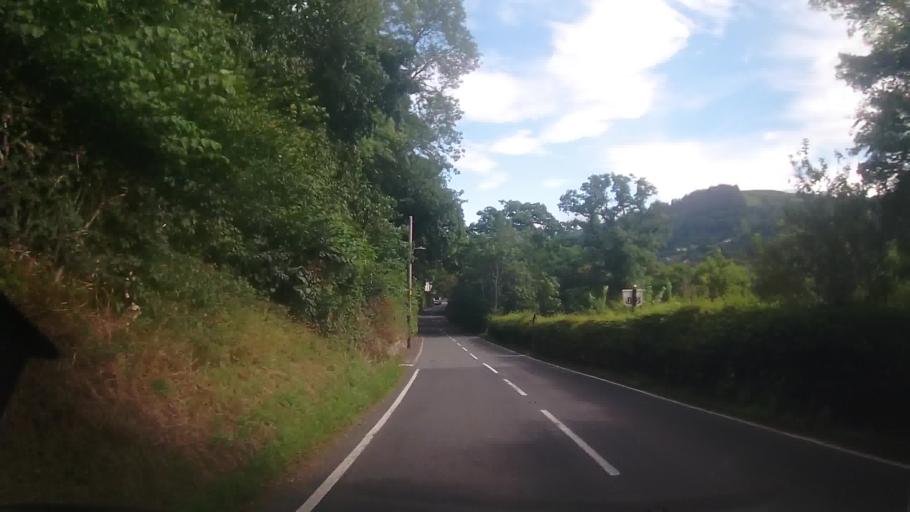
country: GB
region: Wales
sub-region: Denbighshire
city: Llangollen
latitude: 52.9827
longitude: -3.1792
